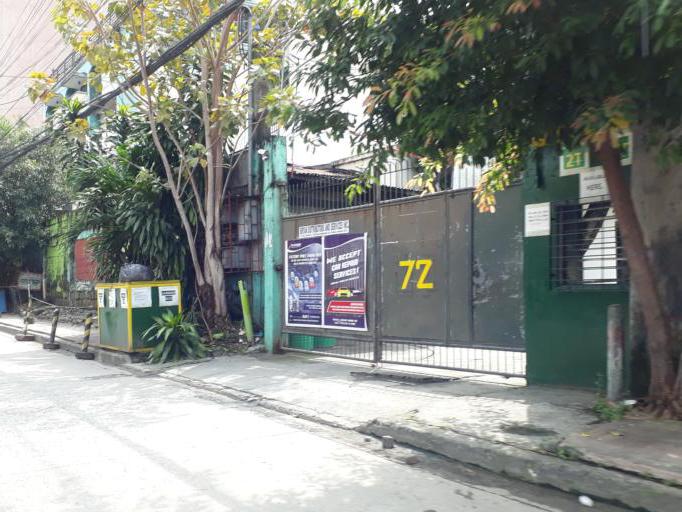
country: PH
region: Metro Manila
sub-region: San Juan
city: San Juan
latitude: 14.6169
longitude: 121.0503
